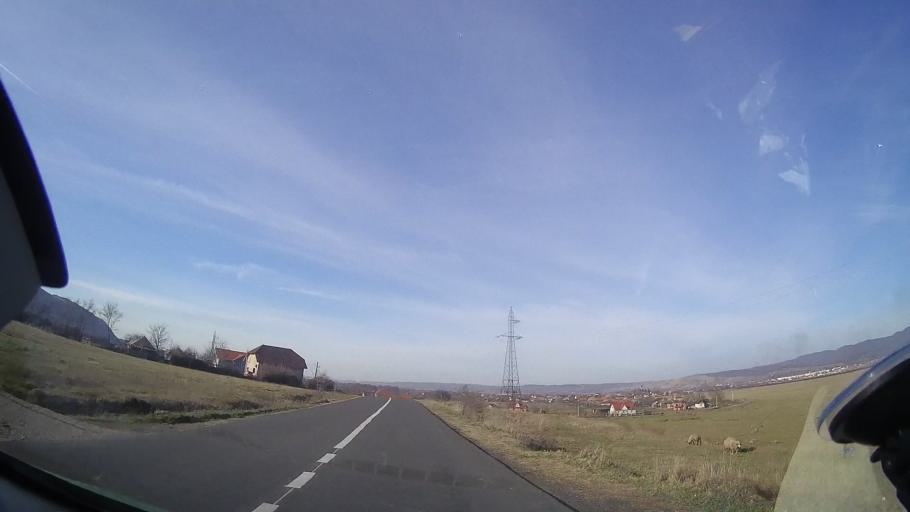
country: RO
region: Bihor
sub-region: Comuna Astileu
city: Astileu
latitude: 47.0255
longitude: 22.4038
